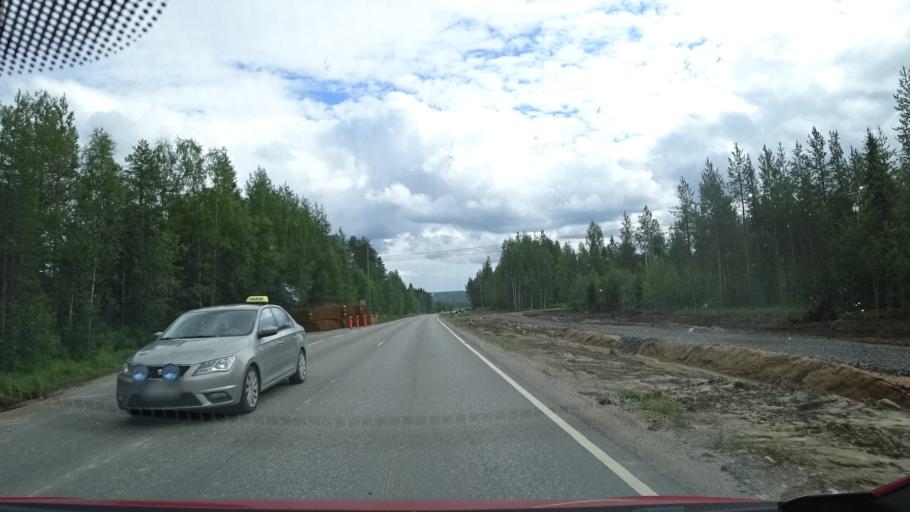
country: FI
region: Lapland
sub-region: Rovaniemi
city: Rovaniemi
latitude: 66.5342
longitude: 25.7312
